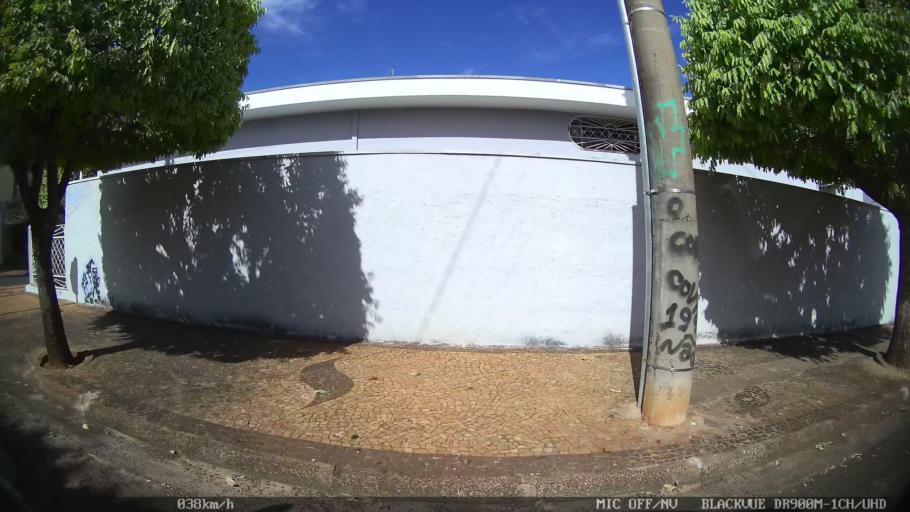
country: BR
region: Sao Paulo
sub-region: Catanduva
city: Catanduva
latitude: -21.1263
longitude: -48.9723
